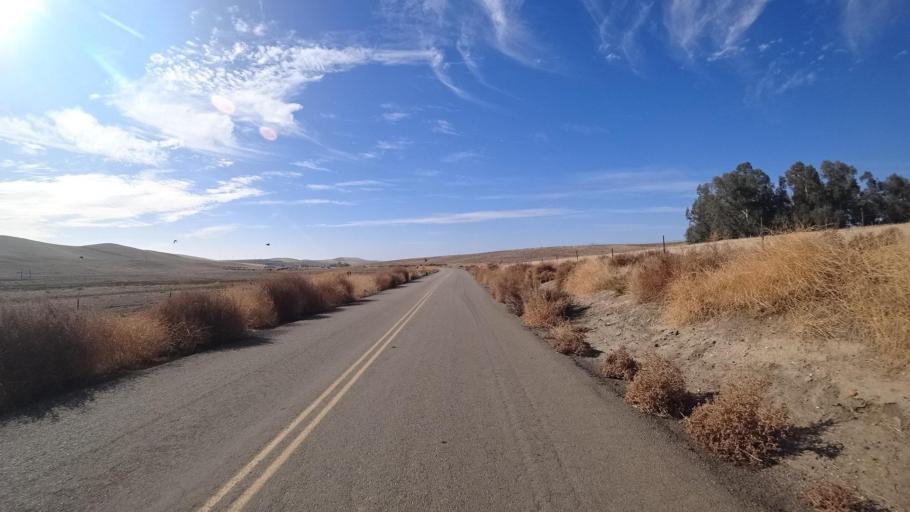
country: US
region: California
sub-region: Tulare County
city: Richgrove
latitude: 35.6309
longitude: -118.9685
